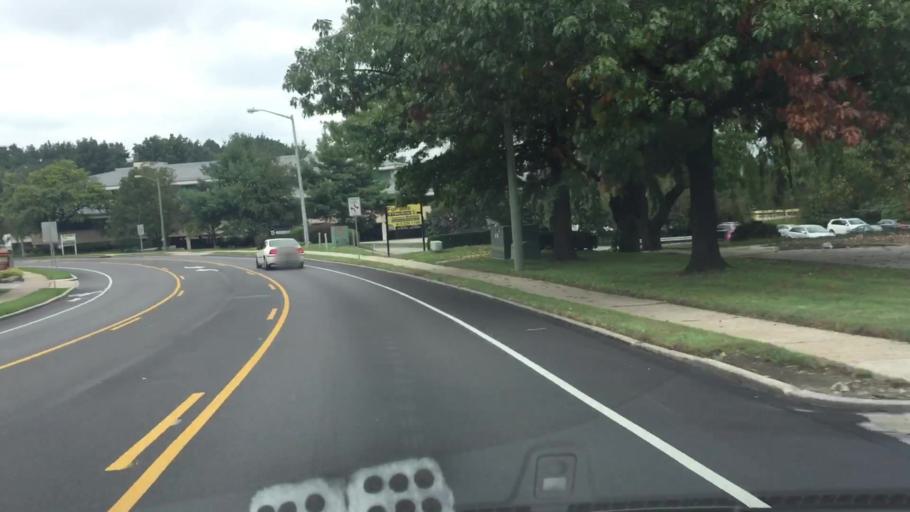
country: US
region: Pennsylvania
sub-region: Montgomery County
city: Bala-Cynwyd
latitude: 40.0112
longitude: -75.2121
